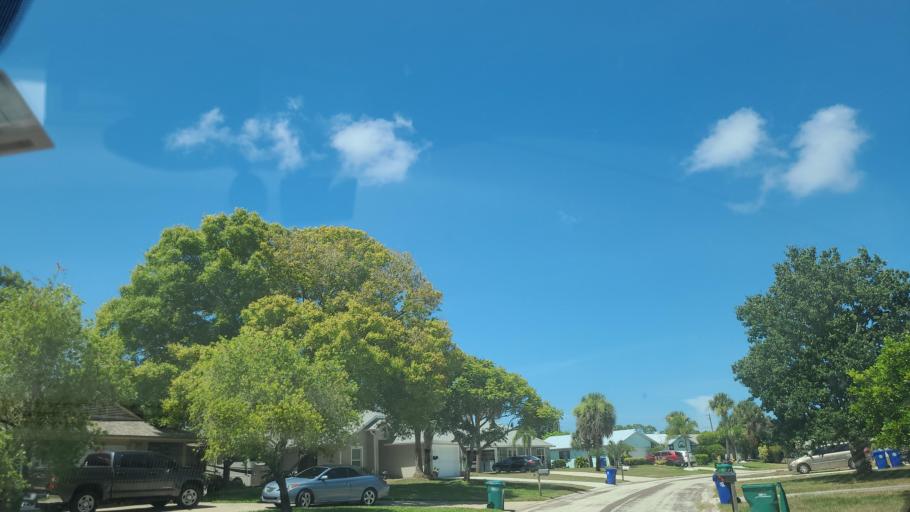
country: US
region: Florida
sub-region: Indian River County
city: Sebastian
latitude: 27.7802
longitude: -80.4666
